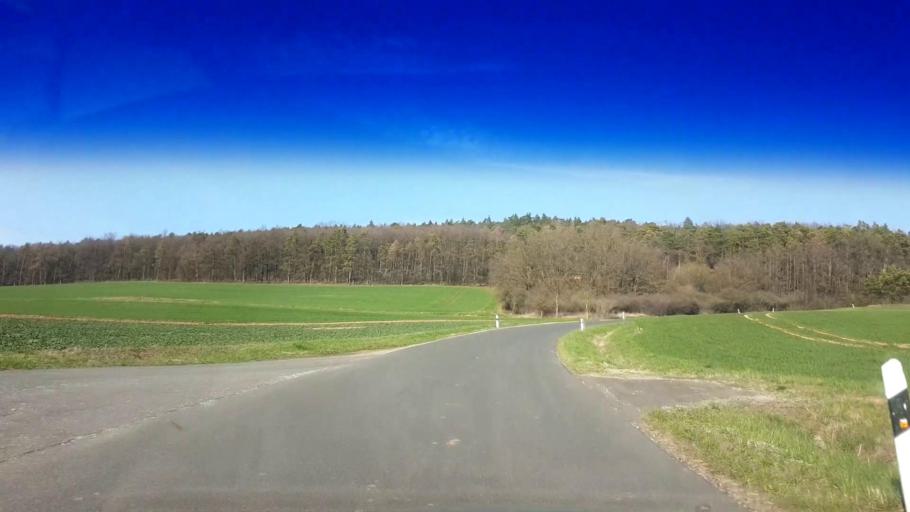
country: DE
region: Bavaria
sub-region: Upper Franconia
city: Rattelsdorf
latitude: 50.0571
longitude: 10.8886
